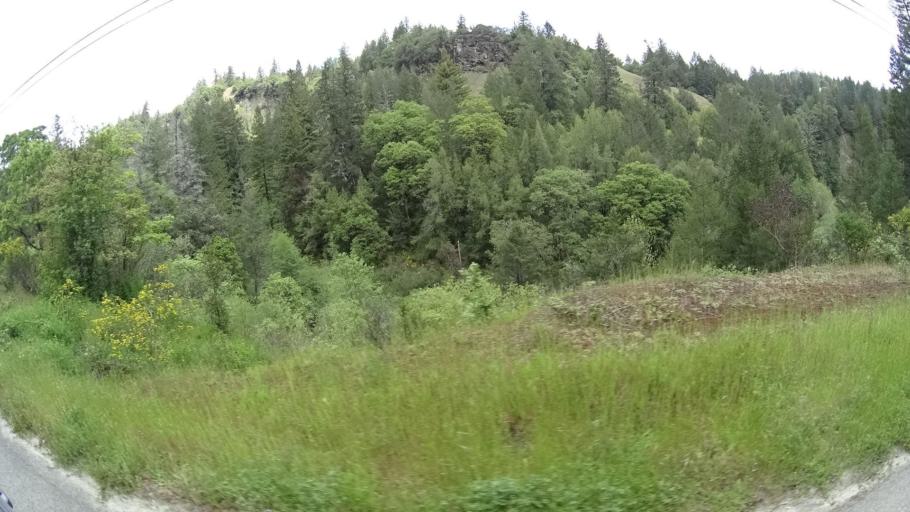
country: US
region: California
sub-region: Humboldt County
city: Redway
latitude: 40.1296
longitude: -123.8562
